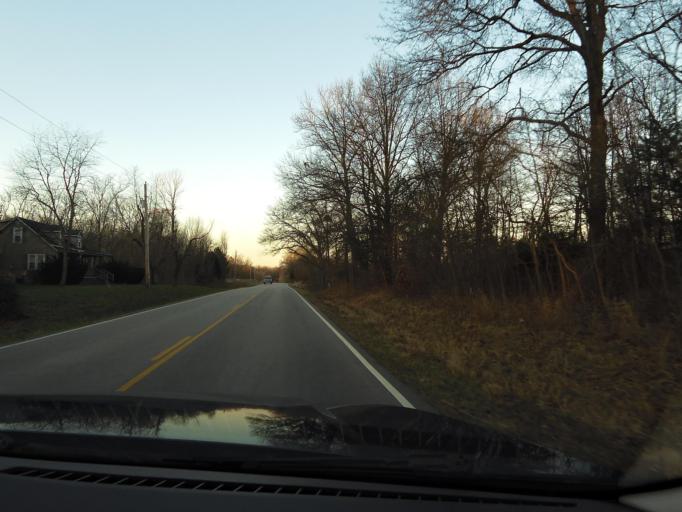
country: US
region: Illinois
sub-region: Marion County
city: Salem
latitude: 38.7584
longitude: -88.9404
